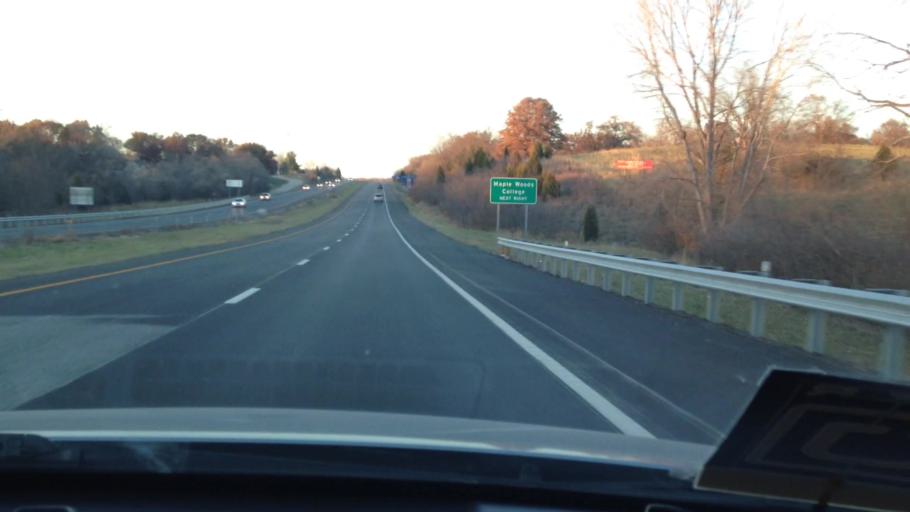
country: US
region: Missouri
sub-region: Clay County
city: Gladstone
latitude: 39.2337
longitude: -94.5894
